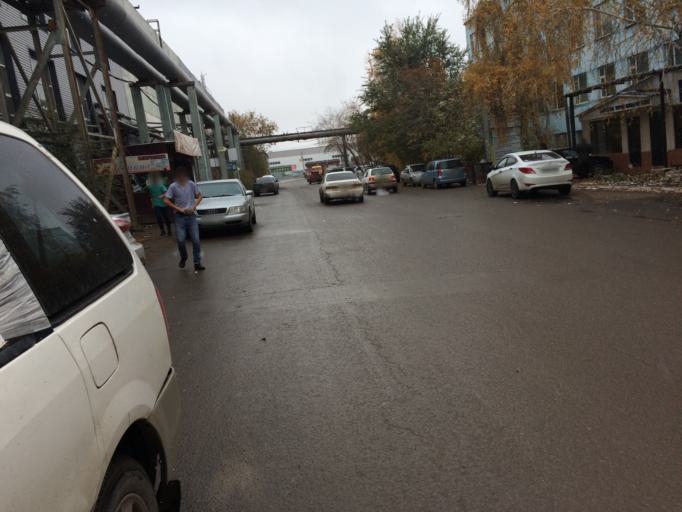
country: KZ
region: Astana Qalasy
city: Astana
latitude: 51.1843
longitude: 71.4312
